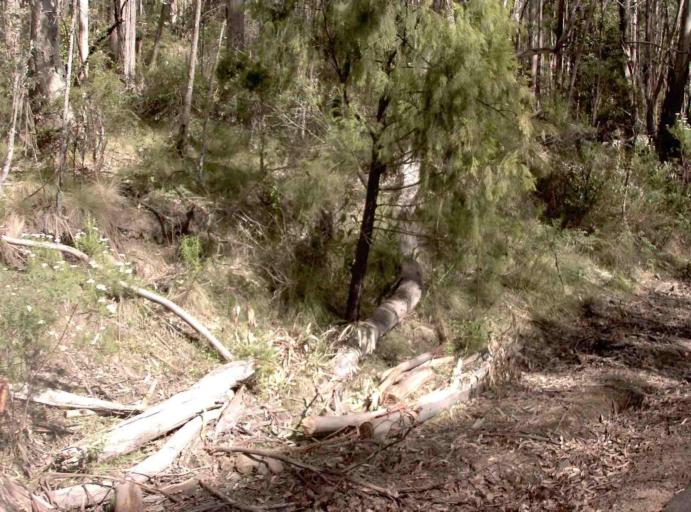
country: AU
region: Victoria
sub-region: East Gippsland
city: Lakes Entrance
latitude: -37.4232
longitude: 148.1282
